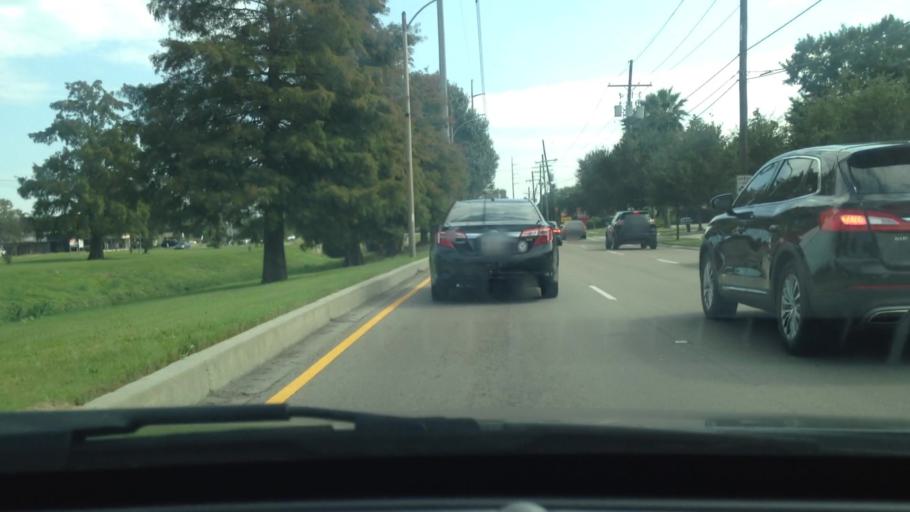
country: US
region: Louisiana
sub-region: Jefferson Parish
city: Terrytown
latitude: 29.9256
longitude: -90.0233
